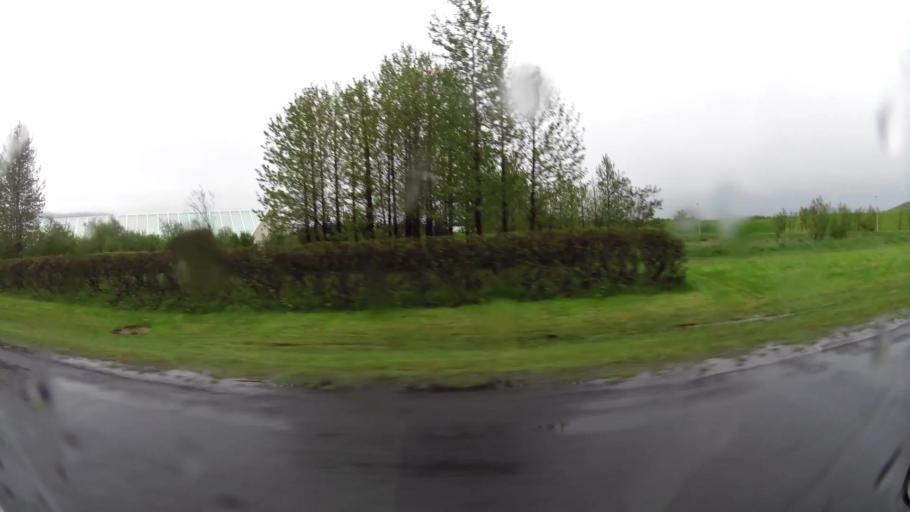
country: IS
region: South
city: Selfoss
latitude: 63.9308
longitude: -20.9969
